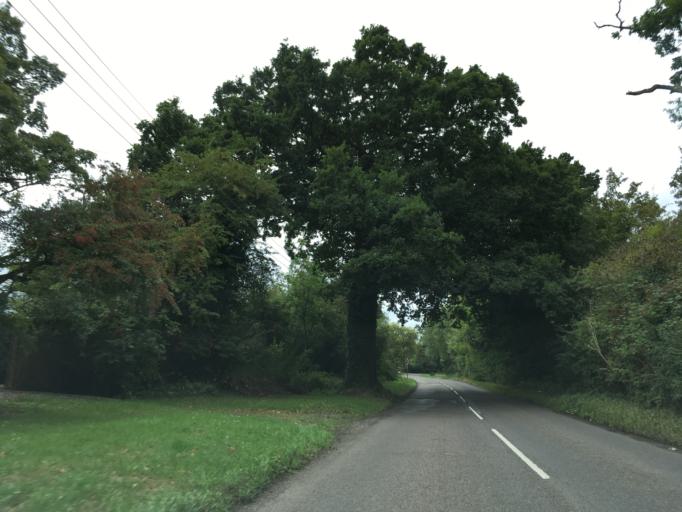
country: GB
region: England
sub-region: South Gloucestershire
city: Siston
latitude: 51.4680
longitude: -2.4555
